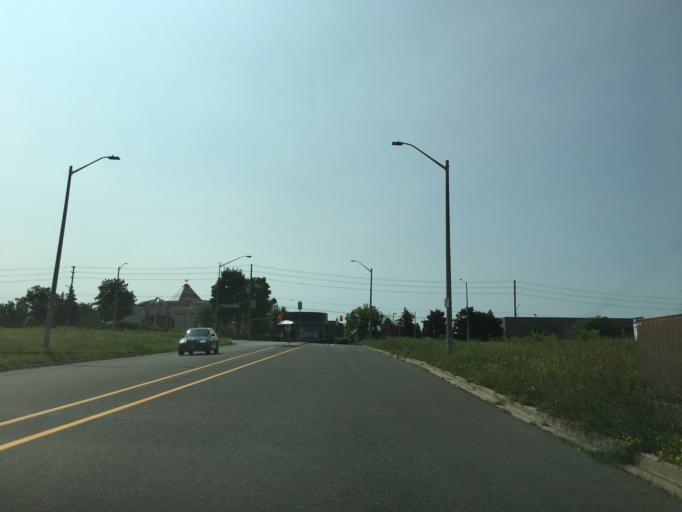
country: CA
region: Ontario
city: Markham
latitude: 43.8431
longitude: -79.3113
